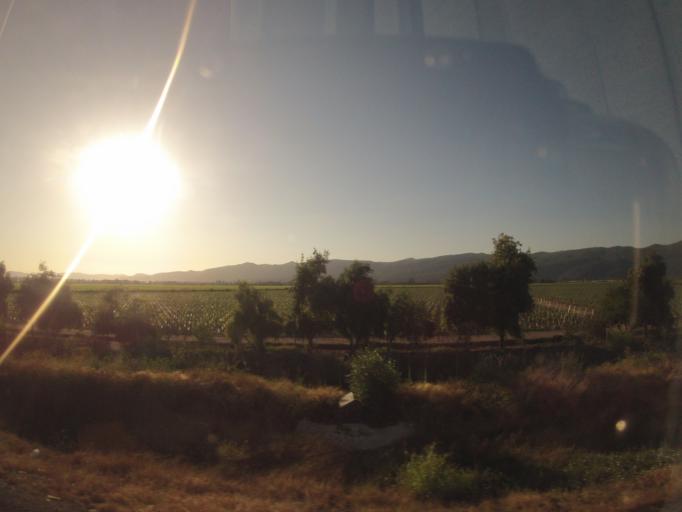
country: CL
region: O'Higgins
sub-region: Provincia de Colchagua
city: Chimbarongo
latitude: -34.7277
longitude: -71.0366
